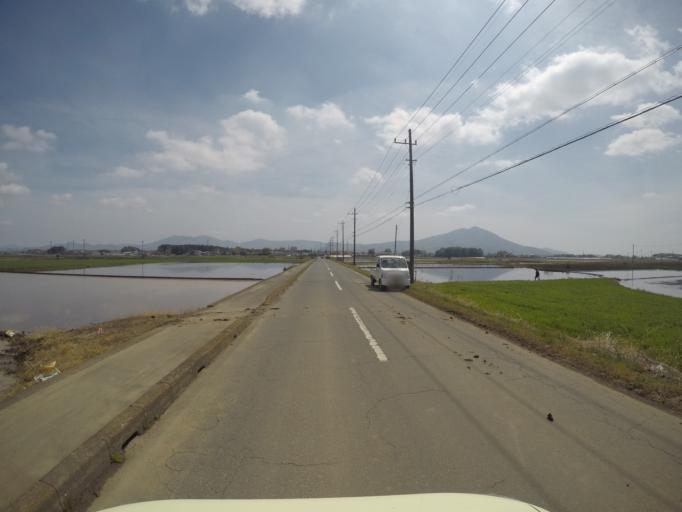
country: JP
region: Ibaraki
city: Shimodate
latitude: 36.2729
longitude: 140.0212
